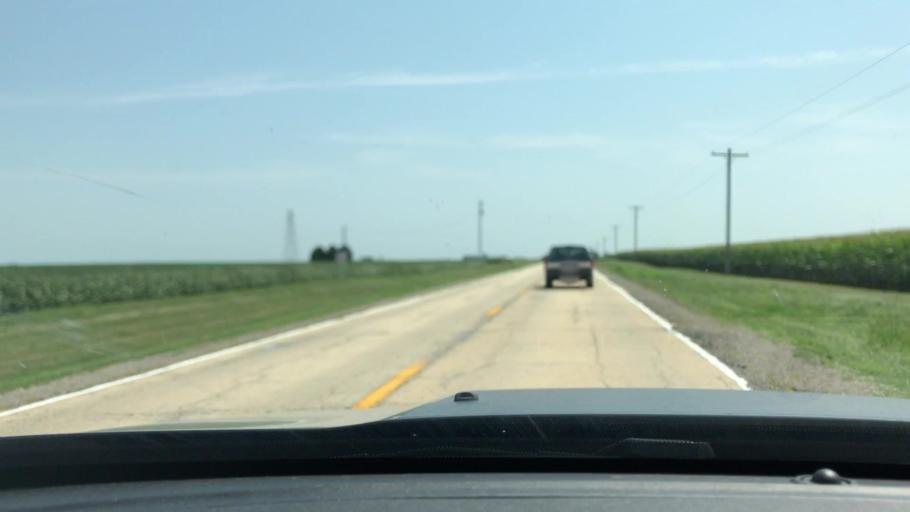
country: US
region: Illinois
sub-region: LaSalle County
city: Earlville
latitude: 41.4693
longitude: -88.9049
